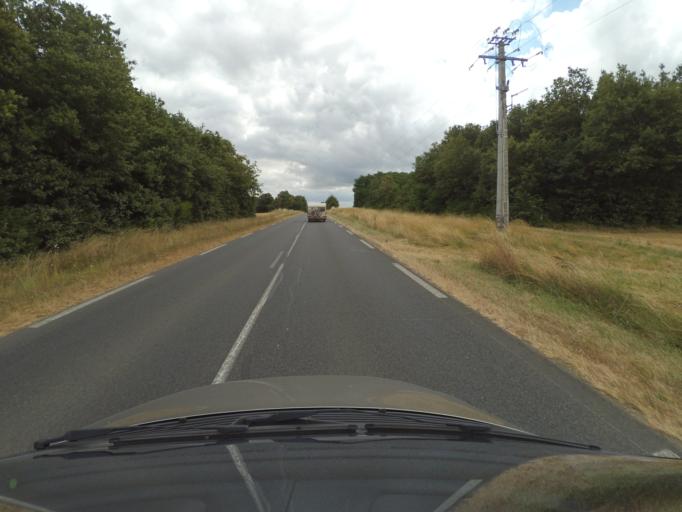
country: FR
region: Centre
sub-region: Departement d'Indre-et-Loire
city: Richelieu
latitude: 47.0080
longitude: 0.2490
